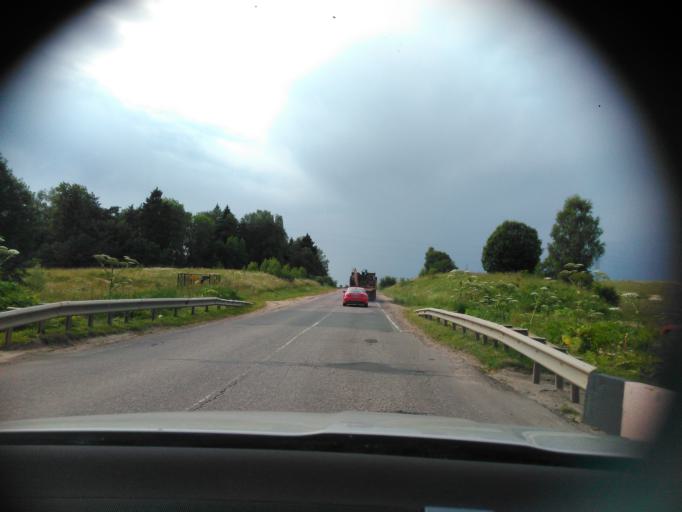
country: RU
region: Moskovskaya
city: Klin
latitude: 56.1487
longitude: 36.7744
